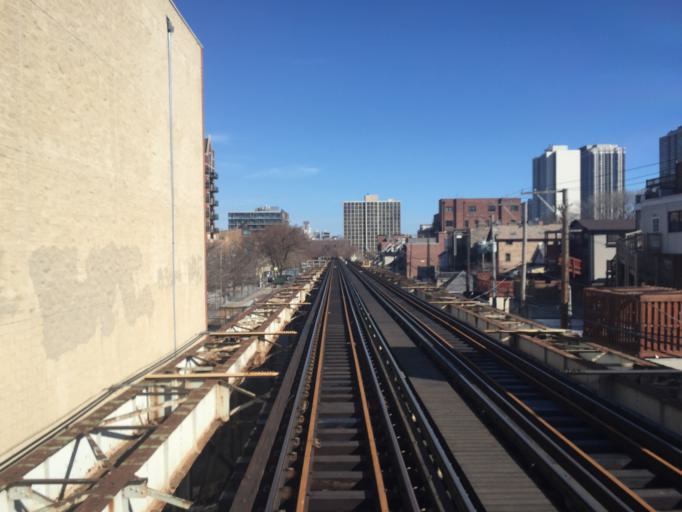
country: US
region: Illinois
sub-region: Cook County
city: Chicago
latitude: 41.9077
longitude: -87.6372
